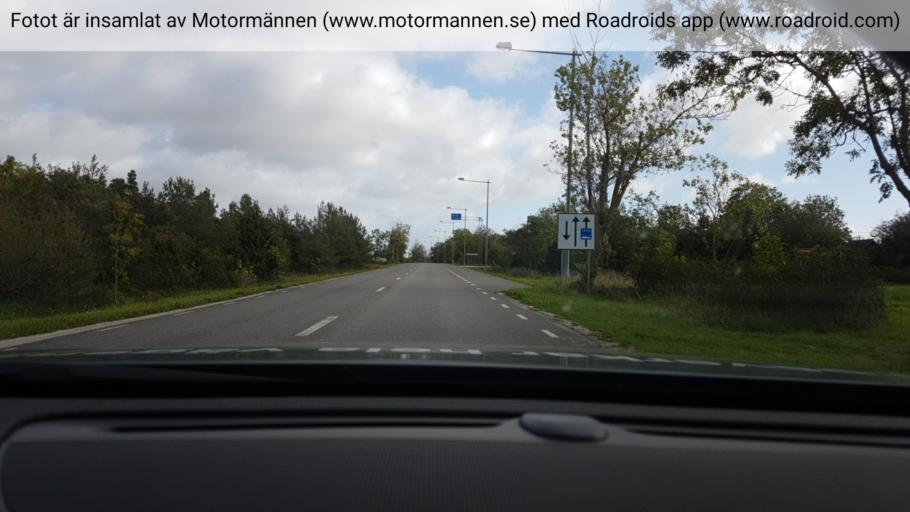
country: SE
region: Gotland
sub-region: Gotland
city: Slite
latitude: 57.8538
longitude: 19.0340
